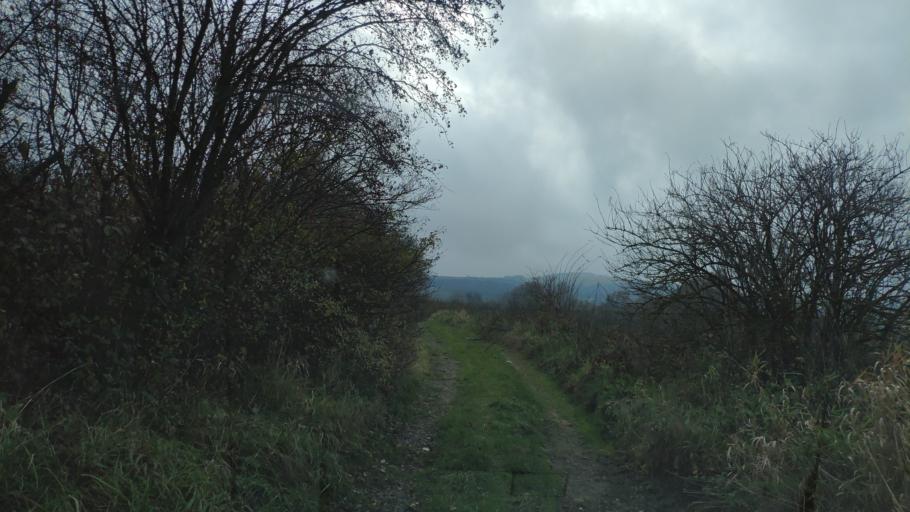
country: SK
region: Presovsky
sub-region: Okres Presov
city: Presov
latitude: 49.0214
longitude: 21.1993
